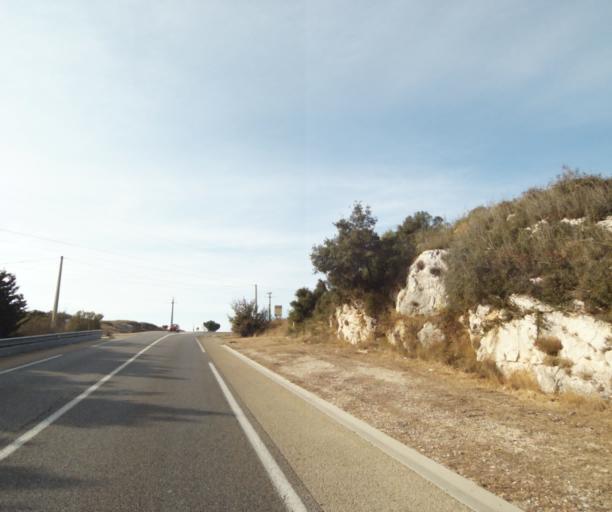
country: FR
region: Provence-Alpes-Cote d'Azur
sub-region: Departement des Bouches-du-Rhone
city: Le Rove
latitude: 43.3611
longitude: 5.2325
